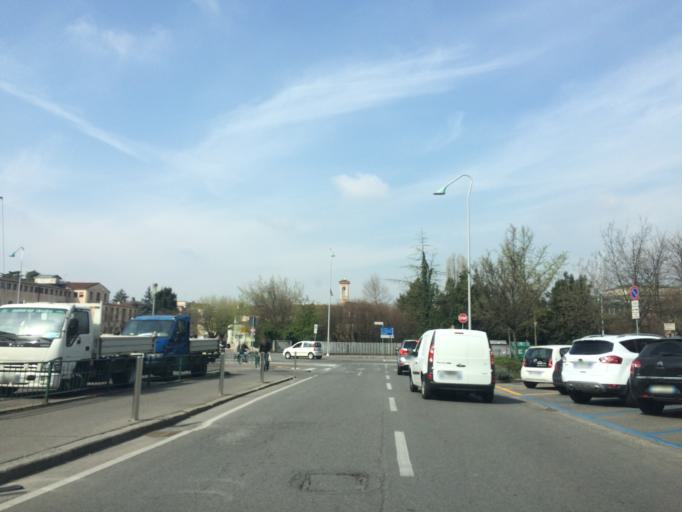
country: IT
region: Lombardy
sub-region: Provincia di Brescia
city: Brescia
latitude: 45.5520
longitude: 10.2286
